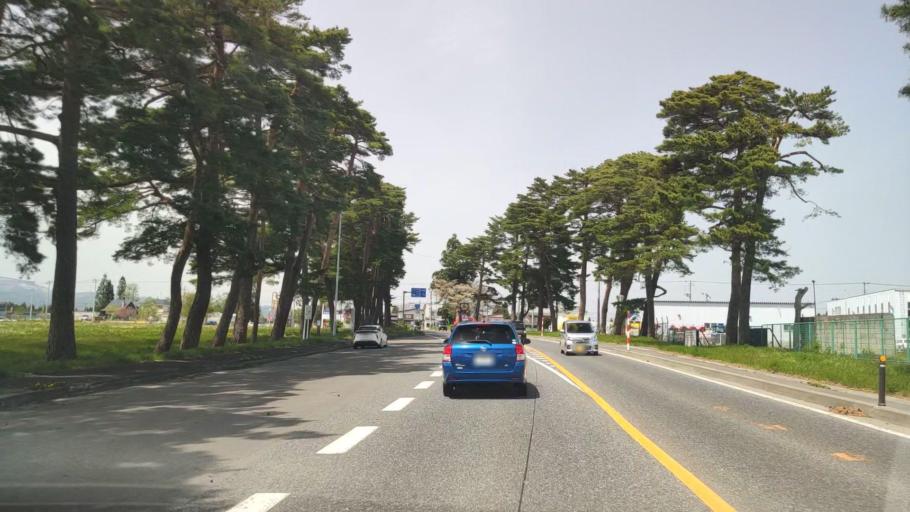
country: JP
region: Aomori
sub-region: Misawa Shi
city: Inuotose
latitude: 40.6718
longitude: 141.1826
